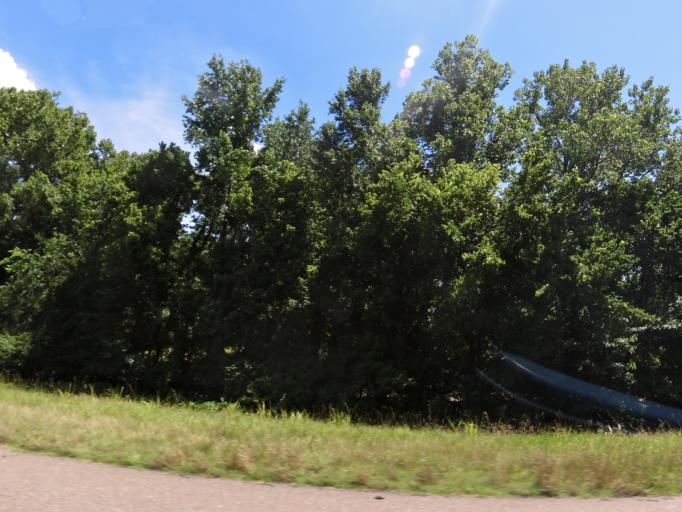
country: US
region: Tennessee
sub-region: Dyer County
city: Dyersburg
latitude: 36.0689
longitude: -89.4157
